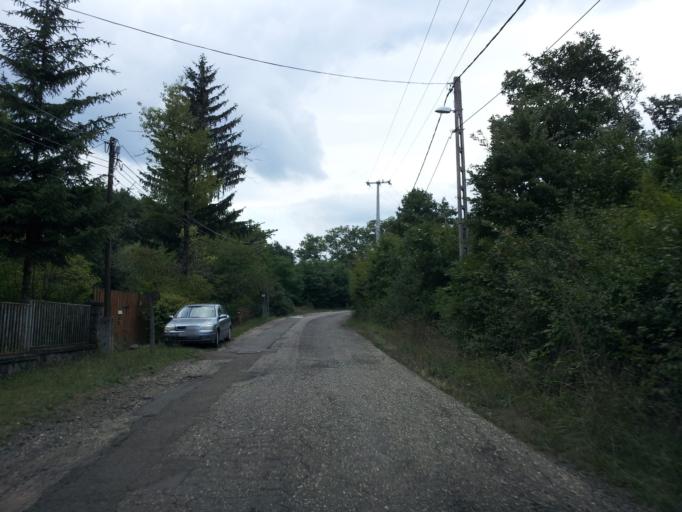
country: HU
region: Pest
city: Kismaros
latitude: 47.8815
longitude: 18.9320
